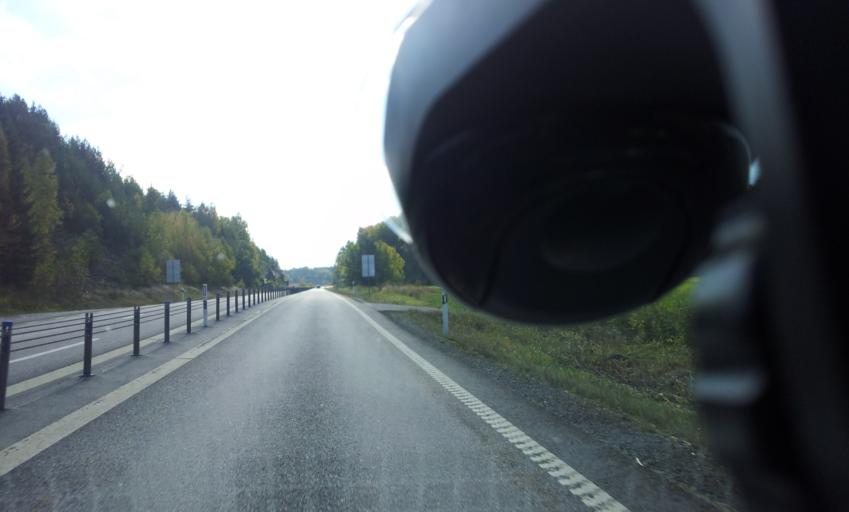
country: SE
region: OEstergoetland
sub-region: Valdemarsviks Kommun
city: Valdemarsvik
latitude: 58.2072
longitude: 16.5571
